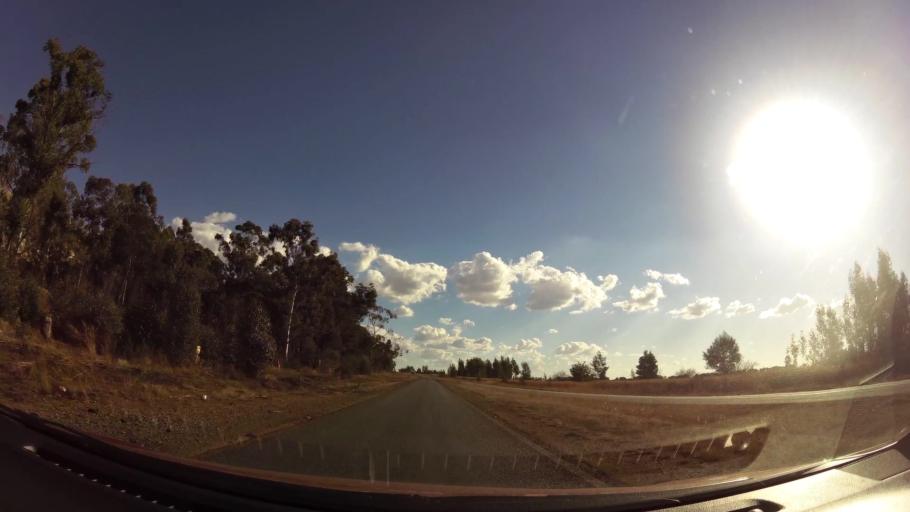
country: ZA
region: Gauteng
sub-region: West Rand District Municipality
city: Carletonville
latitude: -26.3778
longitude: 27.3913
